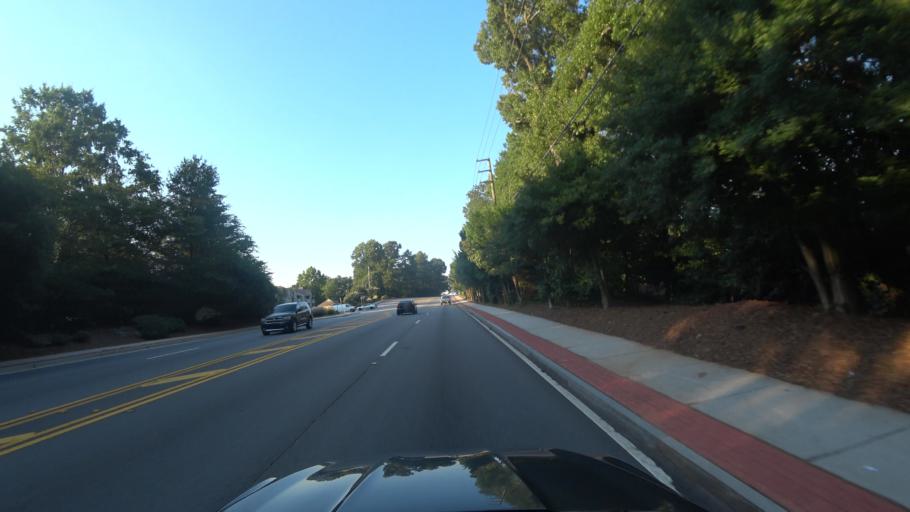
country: US
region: Georgia
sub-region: DeKalb County
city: North Atlanta
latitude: 33.8521
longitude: -84.3147
